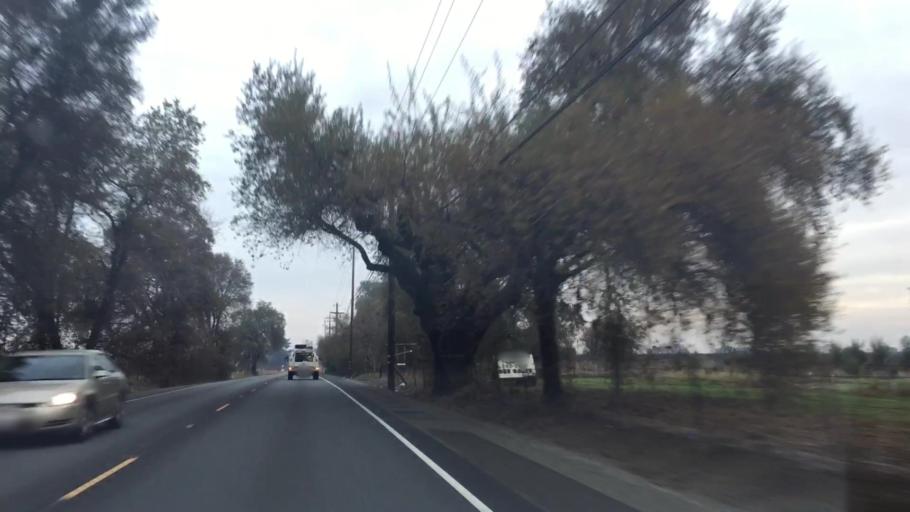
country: US
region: California
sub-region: Sutter County
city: Live Oak
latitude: 39.2769
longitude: -121.5955
